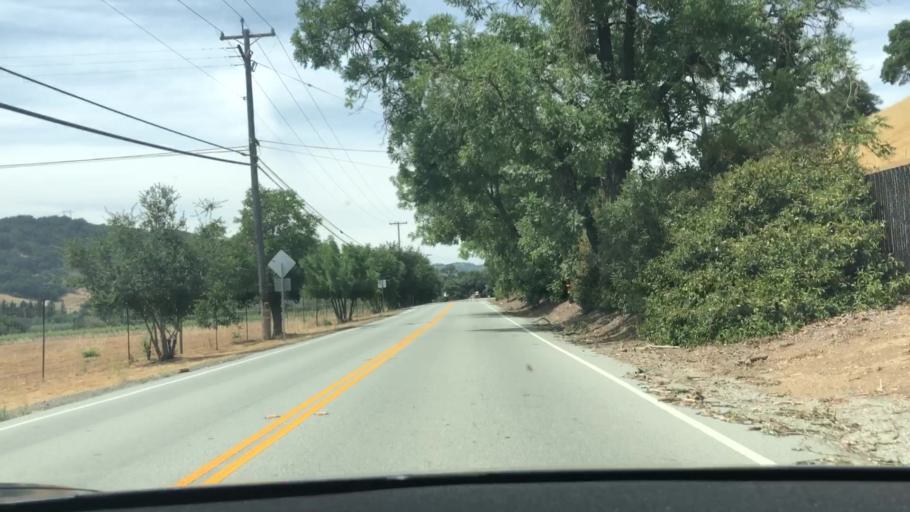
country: US
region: California
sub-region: Santa Clara County
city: San Martin
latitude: 37.0576
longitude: -121.6621
